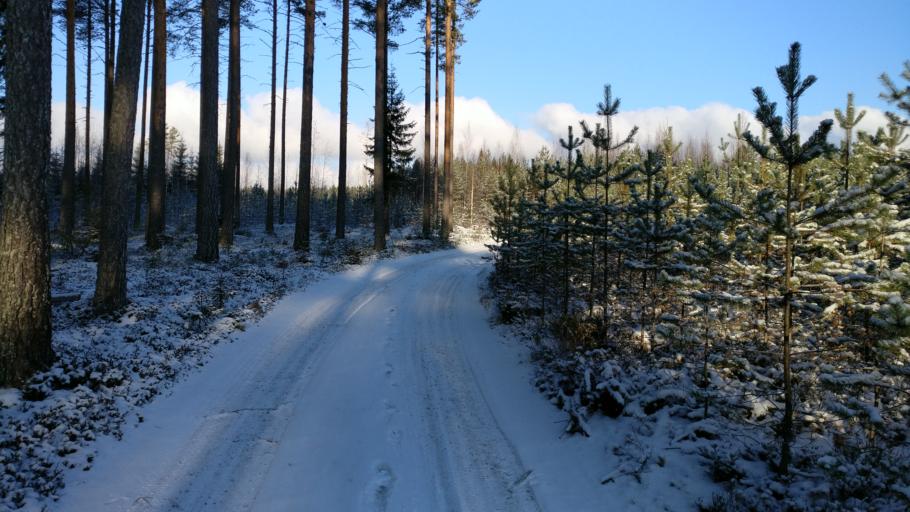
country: FI
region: Central Finland
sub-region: Jyvaeskylae
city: Hankasalmi
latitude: 62.4233
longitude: 26.6746
